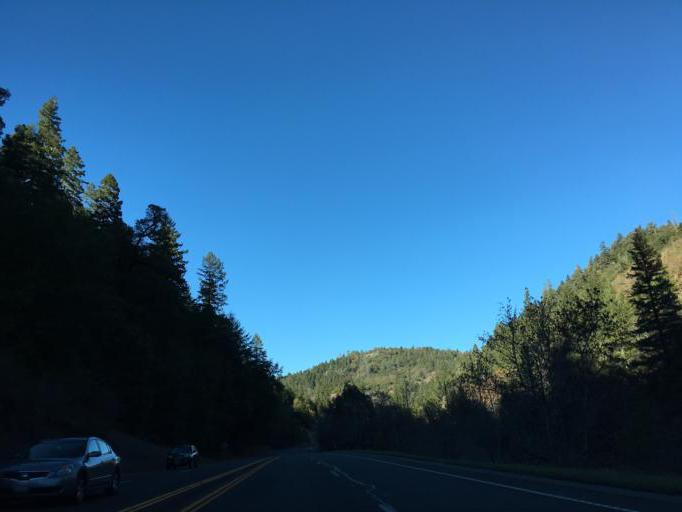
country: US
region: California
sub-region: Mendocino County
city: Brooktrails
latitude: 39.5453
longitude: -123.4243
